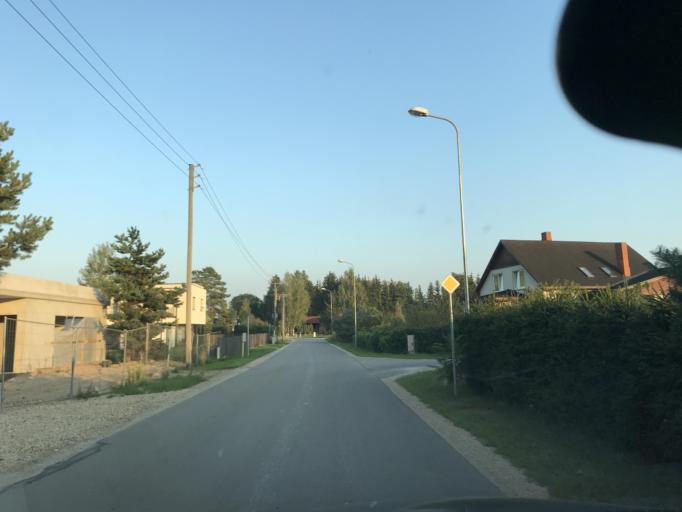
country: LV
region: Ikskile
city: Ikskile
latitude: 56.8241
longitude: 24.5112
